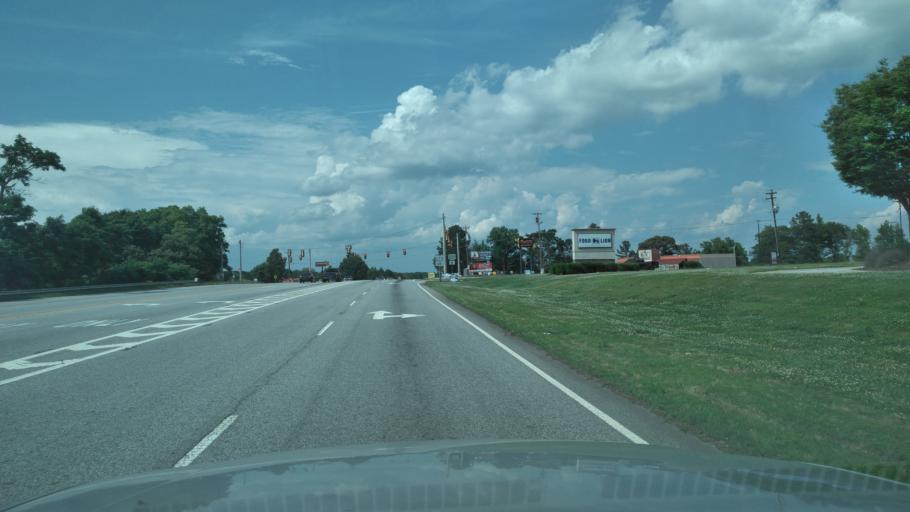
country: US
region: South Carolina
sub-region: Spartanburg County
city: Roebuck
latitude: 34.8703
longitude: -81.9597
